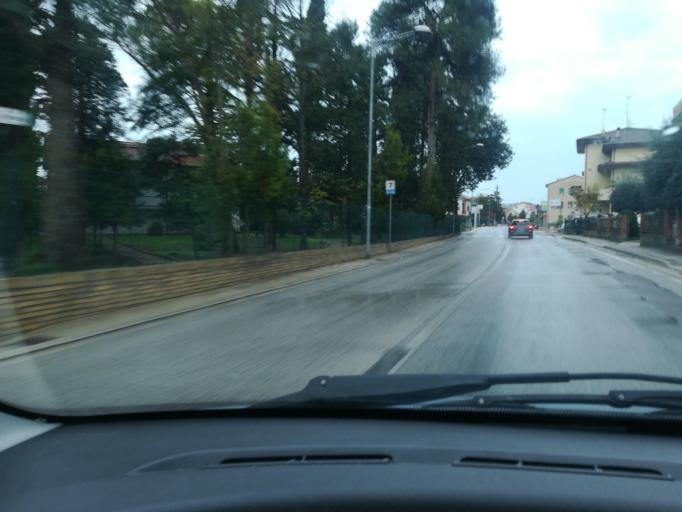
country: IT
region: The Marches
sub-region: Provincia di Macerata
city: Borgo Stazione
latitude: 43.2845
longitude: 13.6428
